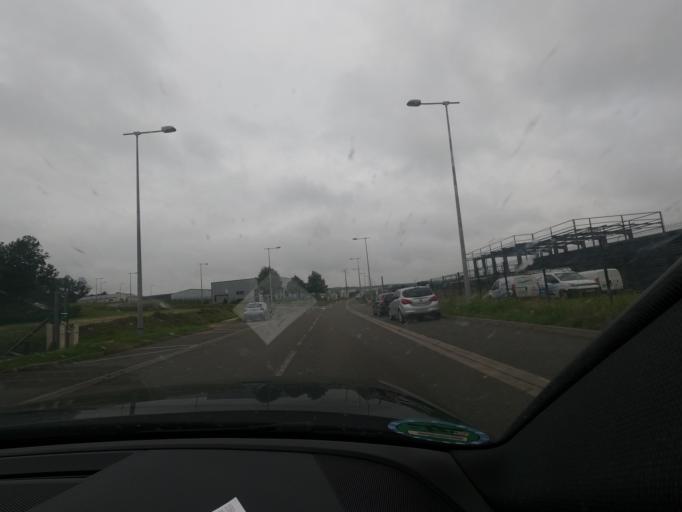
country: FR
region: Picardie
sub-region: Departement de l'Oise
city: Ressons-sur-Matz
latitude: 49.5350
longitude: 2.7387
